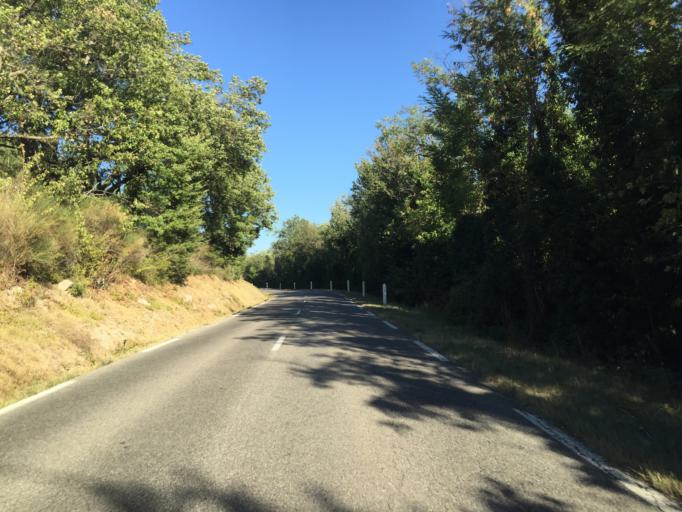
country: FR
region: Provence-Alpes-Cote d'Azur
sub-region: Departement des Alpes-de-Haute-Provence
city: Cereste
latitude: 43.8516
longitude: 5.5252
